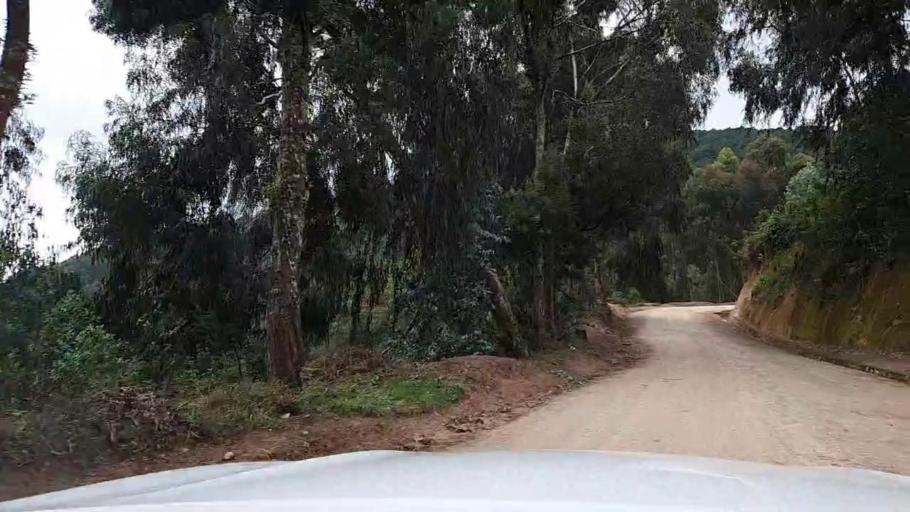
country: RW
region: Southern Province
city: Nzega
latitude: -2.3840
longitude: 29.3844
